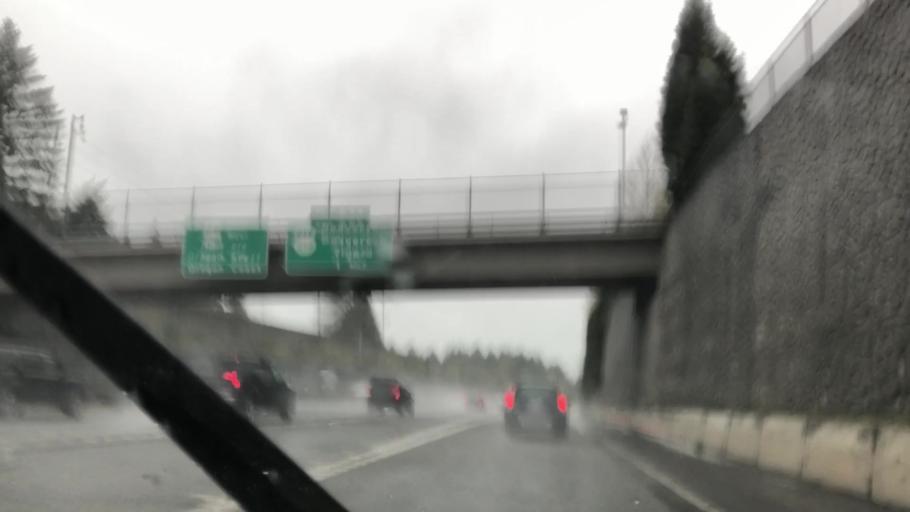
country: US
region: Oregon
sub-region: Washington County
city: West Slope
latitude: 45.5069
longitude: -122.7490
